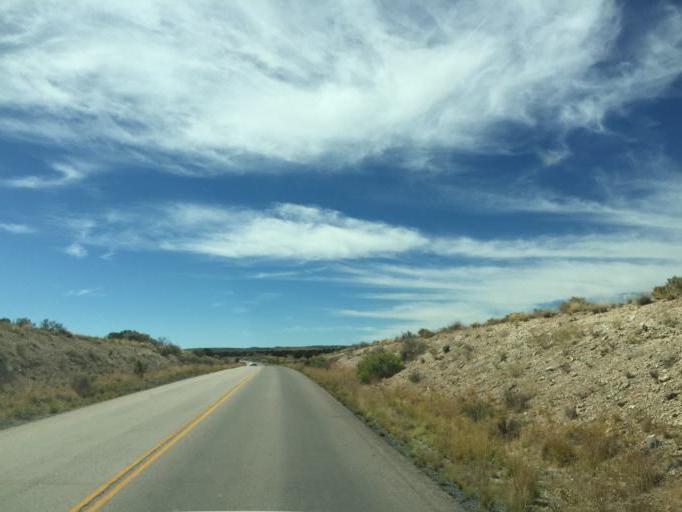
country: US
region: Arizona
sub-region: Mohave County
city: Meadview
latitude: 35.9606
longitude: -113.8326
